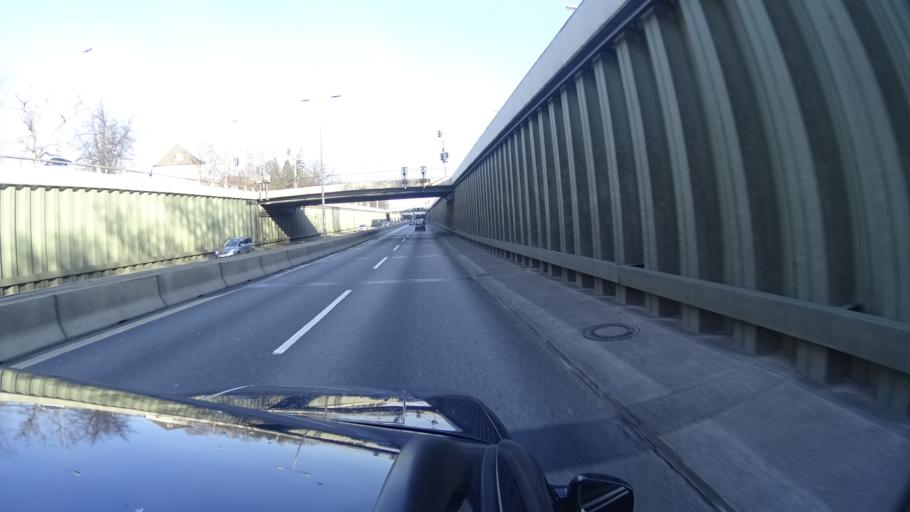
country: DE
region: Berlin
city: Tegel
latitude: 52.5546
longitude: 13.3064
